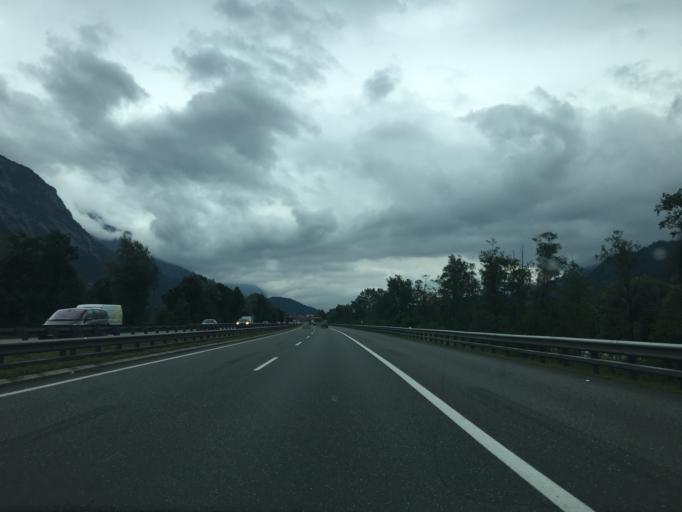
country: AT
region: Tyrol
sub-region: Politischer Bezirk Schwaz
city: Stans
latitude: 47.3670
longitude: 11.7313
